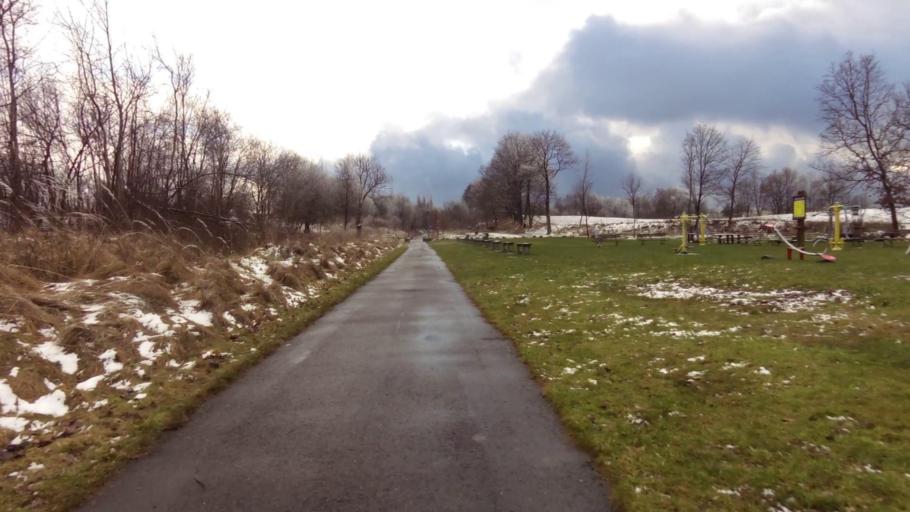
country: PL
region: West Pomeranian Voivodeship
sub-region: Powiat swidwinski
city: Polczyn-Zdroj
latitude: 53.7318
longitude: 16.0431
